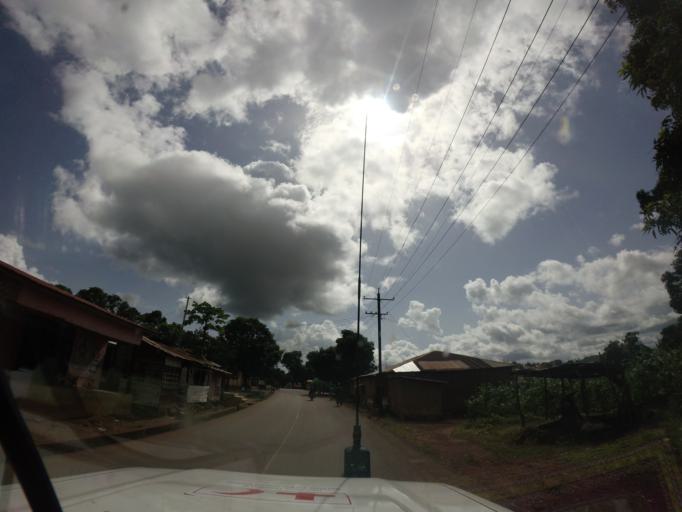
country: GN
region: Mamou
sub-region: Mamou Prefecture
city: Mamou
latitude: 10.3721
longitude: -12.0785
